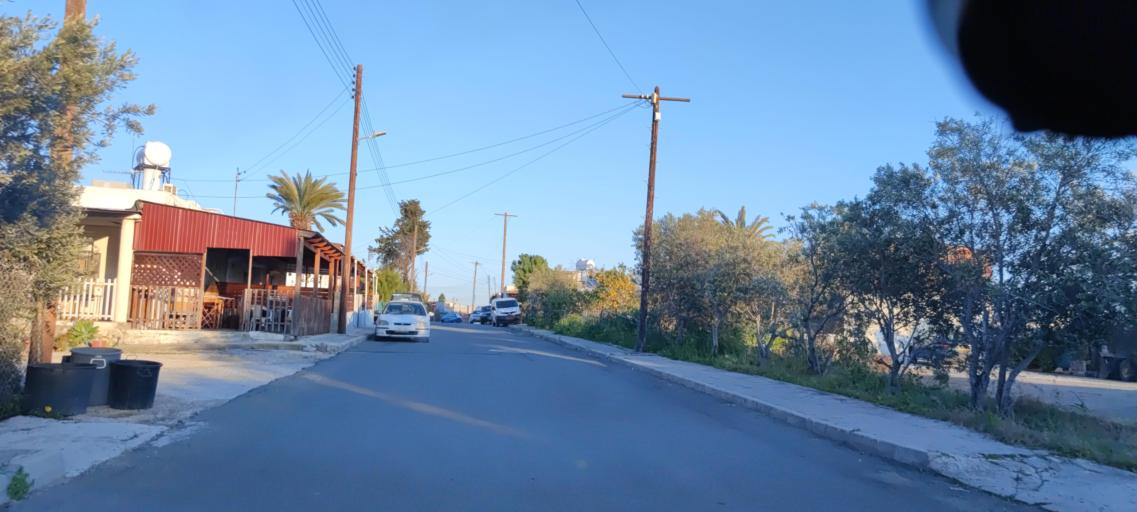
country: CY
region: Pafos
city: Paphos
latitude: 34.7835
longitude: 32.4168
